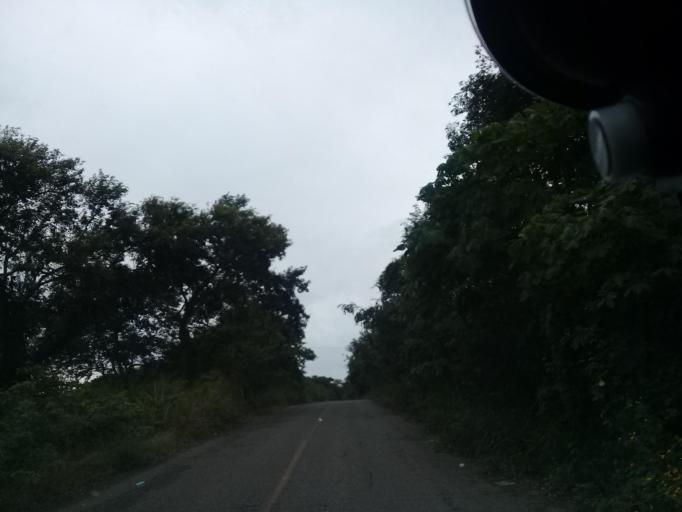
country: MX
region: Hidalgo
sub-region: Huejutla de Reyes
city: Chalahuiyapa
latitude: 21.1998
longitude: -98.3484
